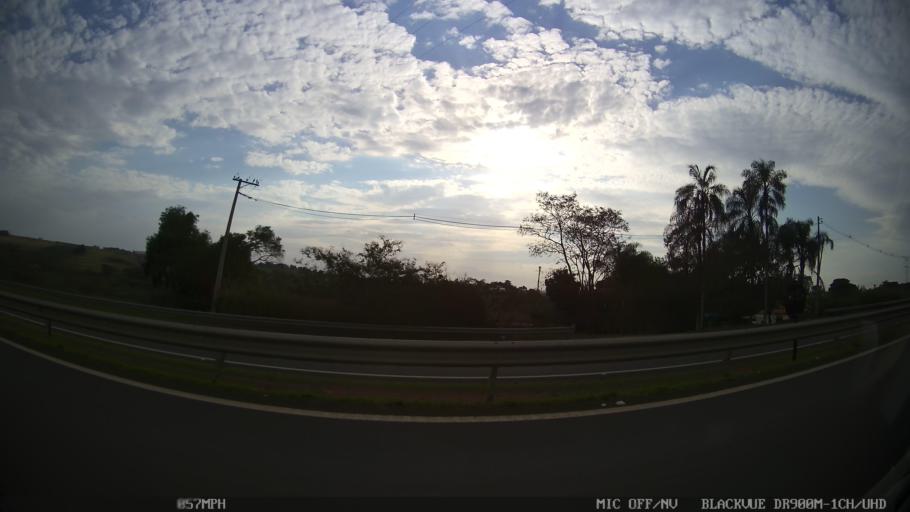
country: BR
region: Sao Paulo
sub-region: Cosmopolis
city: Cosmopolis
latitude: -22.6125
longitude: -47.1954
